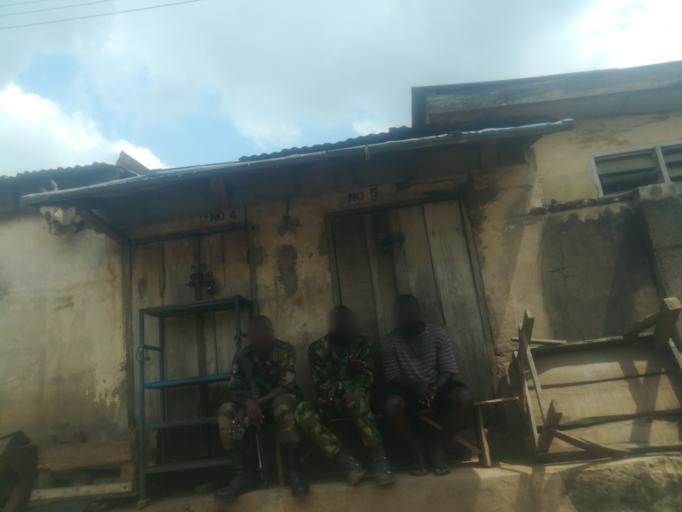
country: NG
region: Oyo
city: Ibadan
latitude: 7.3951
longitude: 3.9191
